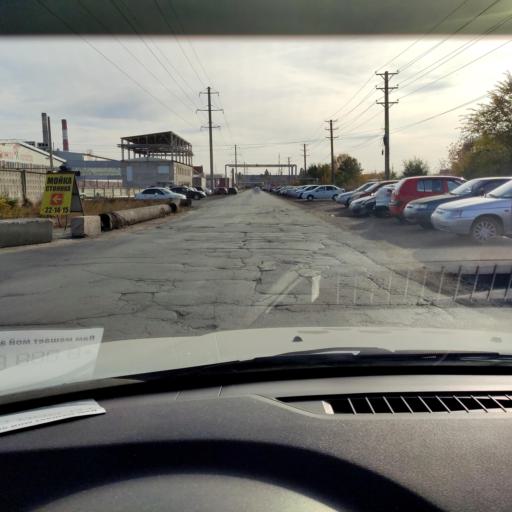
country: RU
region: Samara
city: Tol'yatti
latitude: 53.5463
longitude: 49.4355
